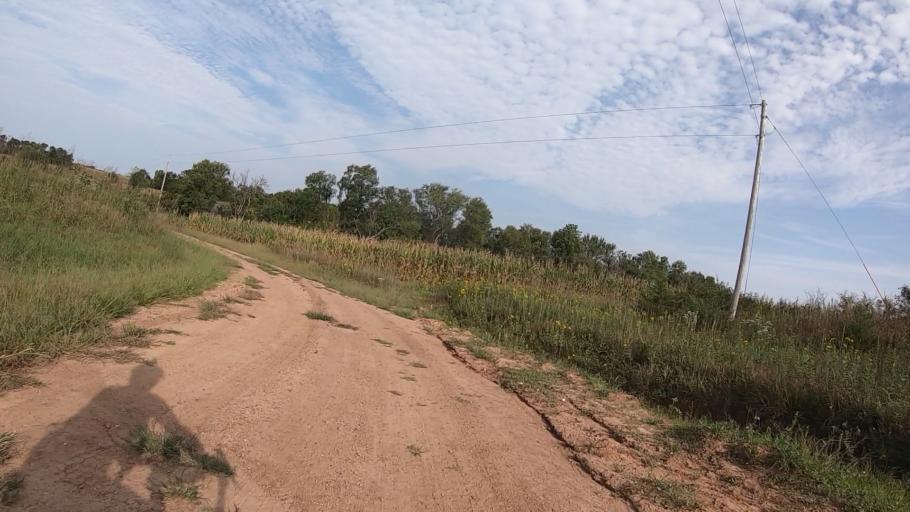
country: US
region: Kansas
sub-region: Washington County
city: Washington
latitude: 39.6750
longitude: -96.9472
